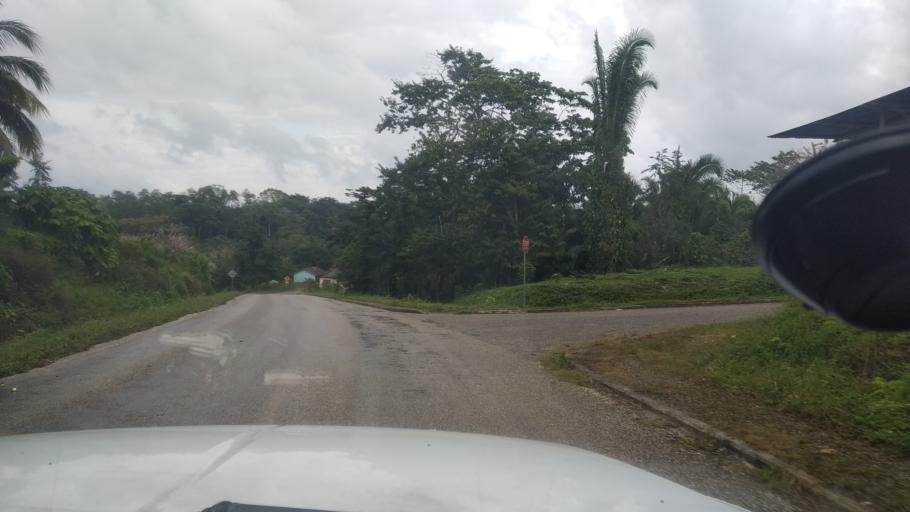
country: GT
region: Peten
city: San Luis
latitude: 16.2019
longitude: -89.1444
